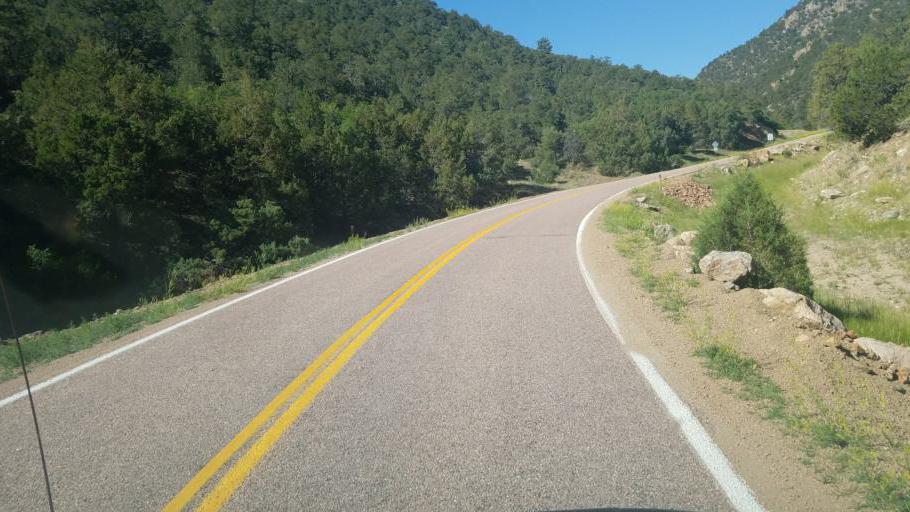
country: US
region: Colorado
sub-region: Fremont County
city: Canon City
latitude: 38.4218
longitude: -105.4066
